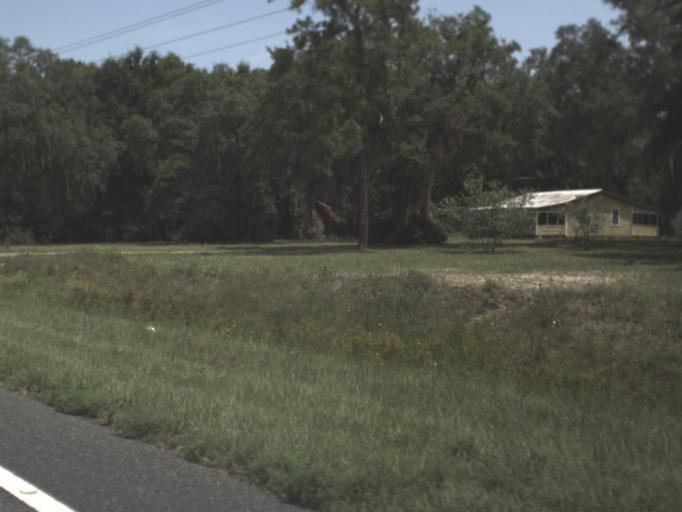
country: US
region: Florida
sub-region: Taylor County
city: Perry
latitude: 30.0350
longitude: -83.5443
